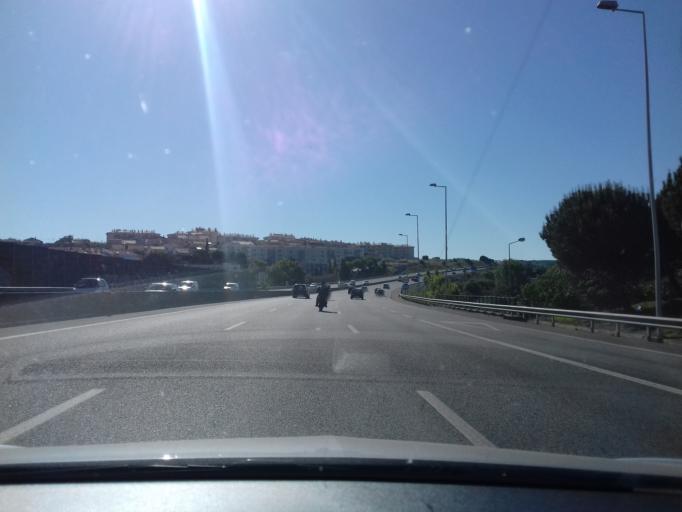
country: PT
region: Lisbon
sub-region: Cascais
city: Sao Domingos de Rana
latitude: 38.7081
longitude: -9.3439
